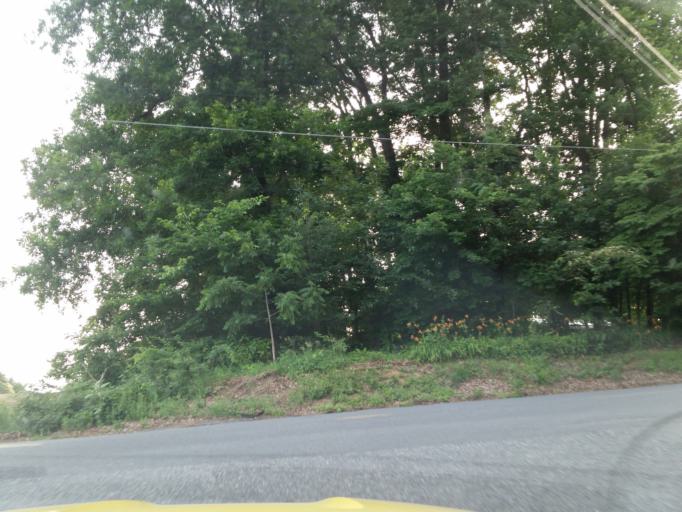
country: US
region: Pennsylvania
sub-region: Lebanon County
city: Fredericksburg
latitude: 40.4451
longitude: -76.4002
